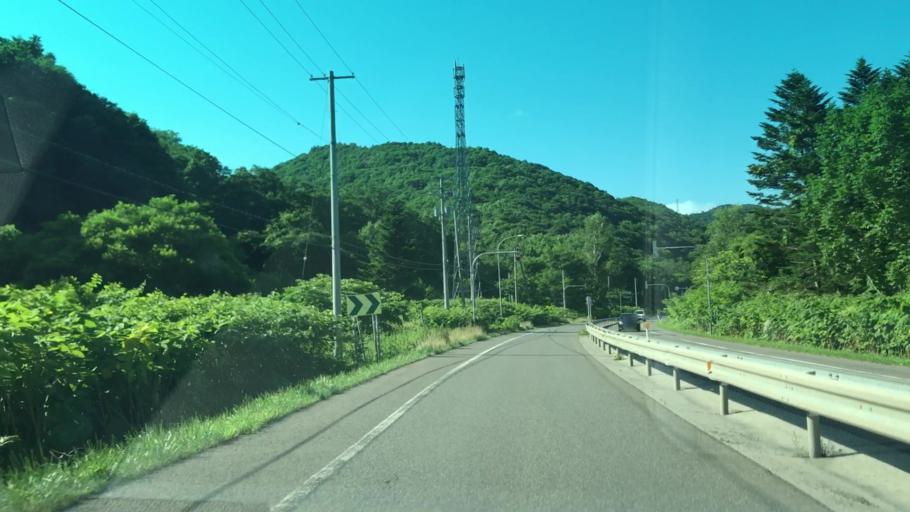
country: JP
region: Hokkaido
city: Iwanai
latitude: 43.0076
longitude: 140.6657
